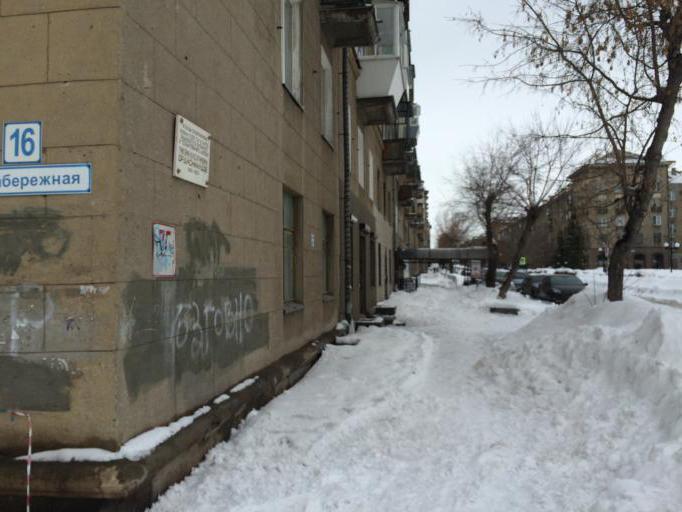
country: RU
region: Chelyabinsk
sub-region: Gorod Magnitogorsk
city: Magnitogorsk
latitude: 53.4177
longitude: 59.0013
